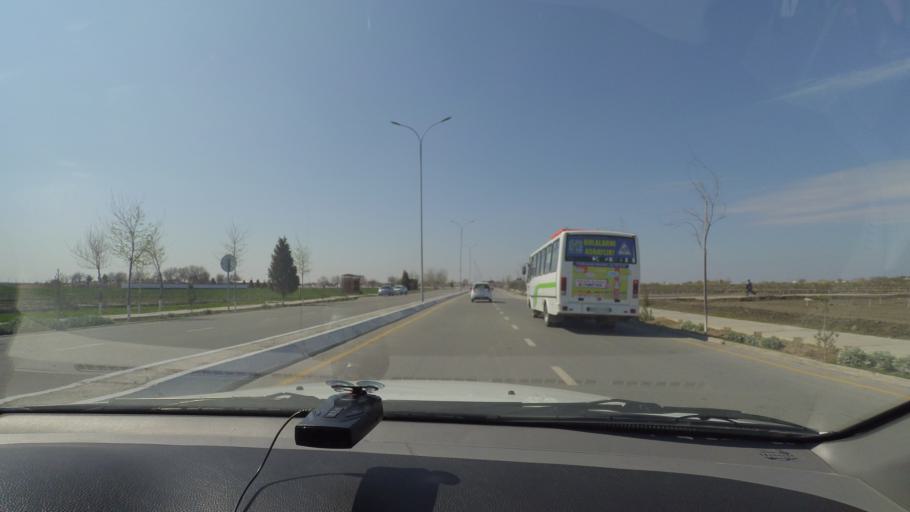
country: UZ
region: Bukhara
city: Bukhara
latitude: 39.7973
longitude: 64.4818
